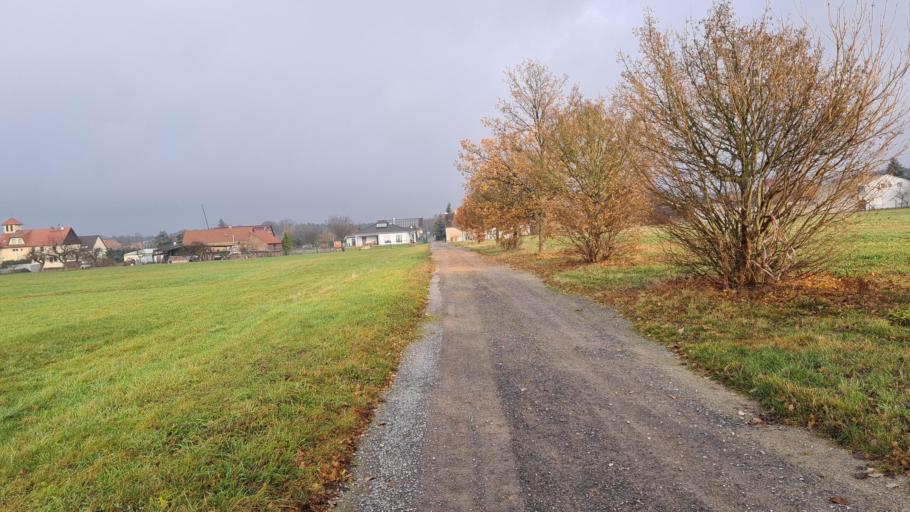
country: DE
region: Brandenburg
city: Sallgast
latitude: 51.5939
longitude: 13.7799
